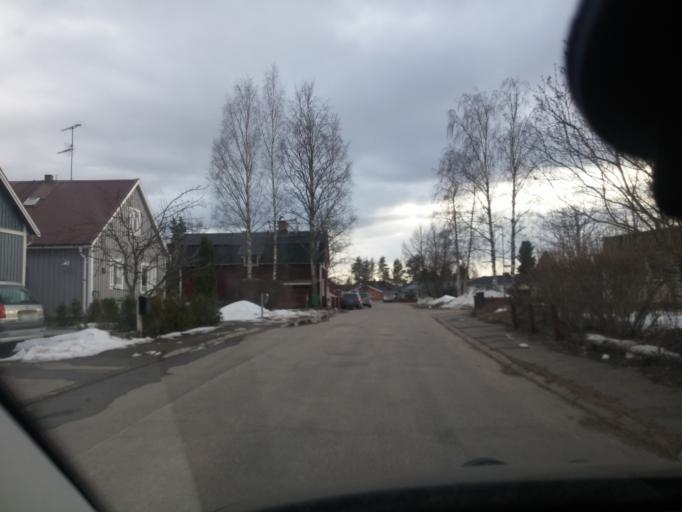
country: SE
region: Gaevleborg
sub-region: Ljusdals Kommun
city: Ljusdal
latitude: 61.8337
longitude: 16.0981
